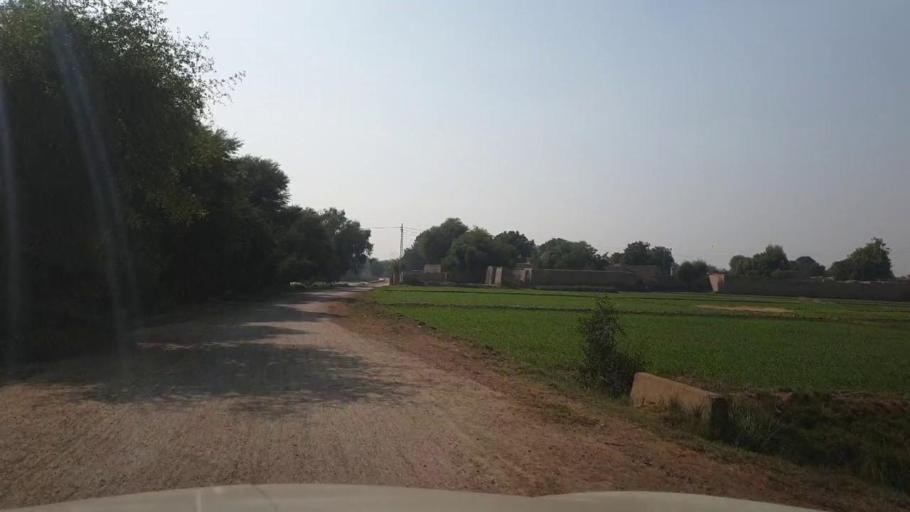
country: PK
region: Sindh
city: Bhan
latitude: 26.5173
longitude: 67.7785
